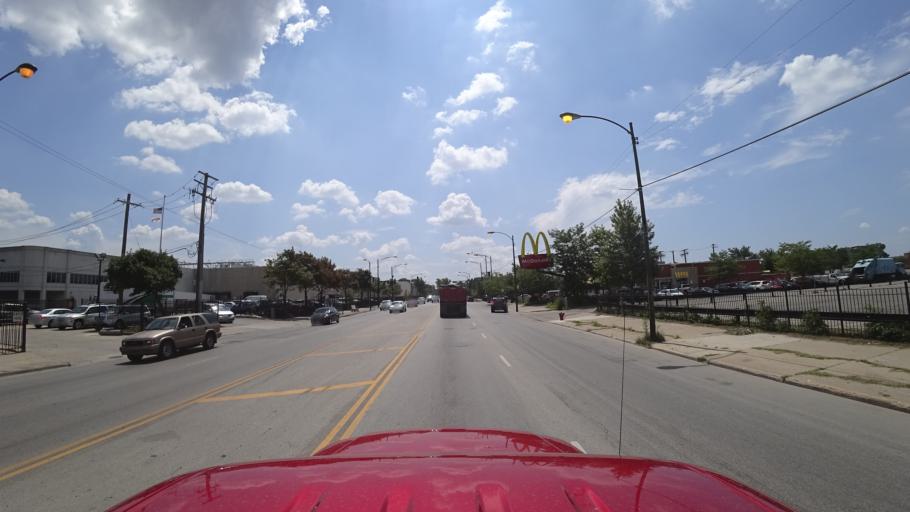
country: US
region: Illinois
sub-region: Cook County
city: Chicago
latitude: 41.8187
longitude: -87.6653
